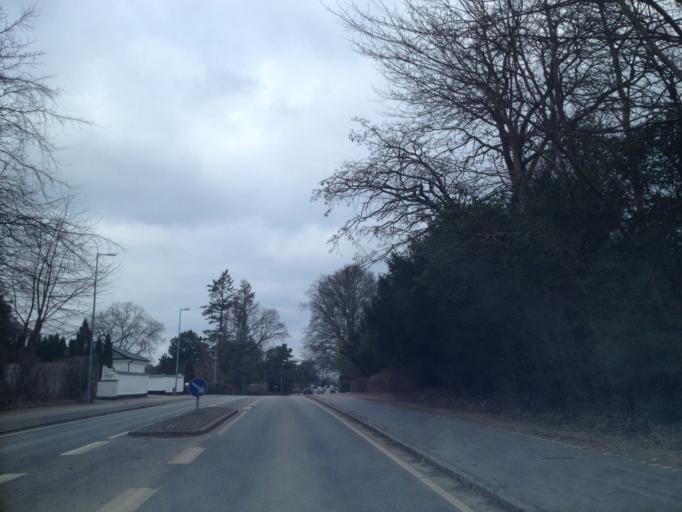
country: DK
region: Capital Region
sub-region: Rudersdal Kommune
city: Trorod
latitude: 55.8700
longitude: 12.5502
